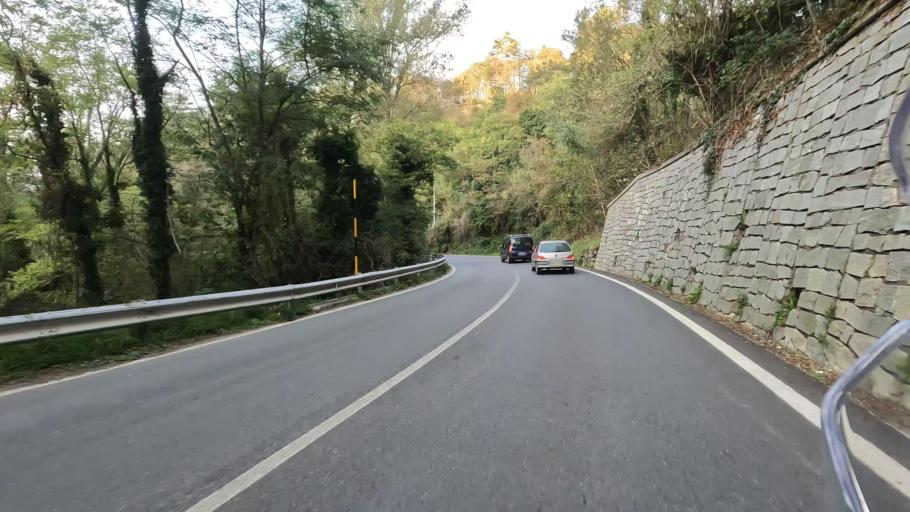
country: IT
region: Liguria
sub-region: Provincia di Savona
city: Osteria dei Cacciatori-Stella
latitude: 44.4124
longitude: 8.4843
